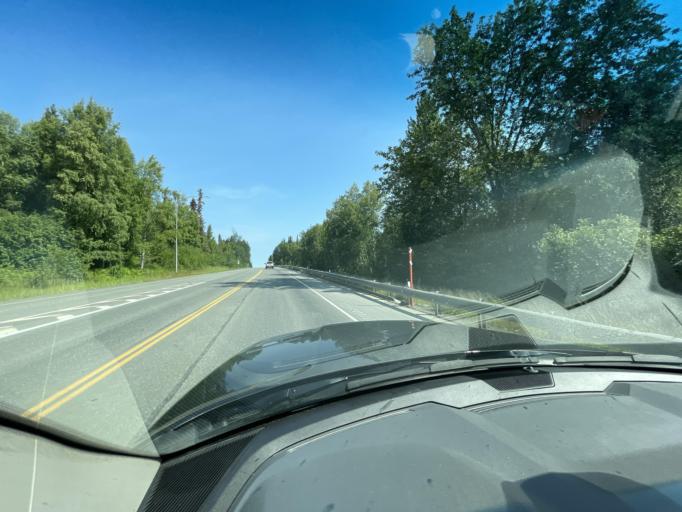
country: US
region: Alaska
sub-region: Kenai Peninsula Borough
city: Soldotna
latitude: 60.4567
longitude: -151.0983
